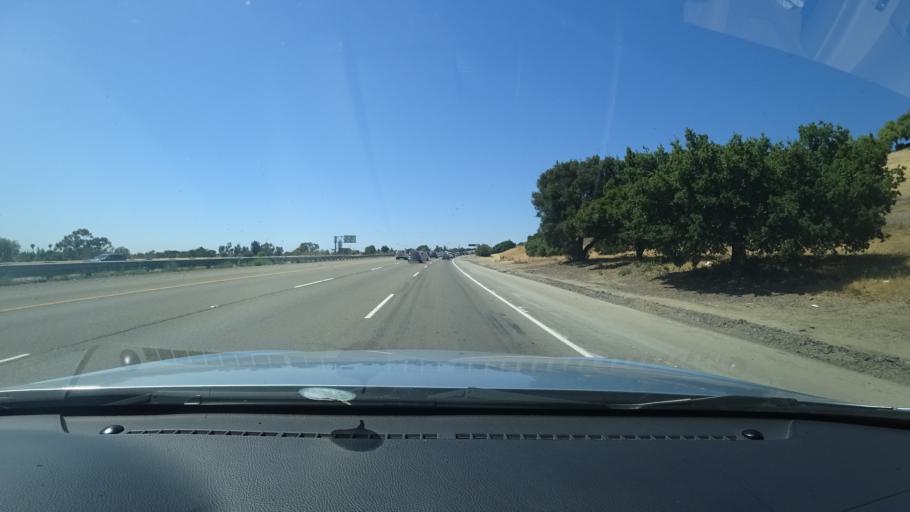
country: US
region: California
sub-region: Santa Clara County
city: Milpitas
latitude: 37.4716
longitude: -121.9094
